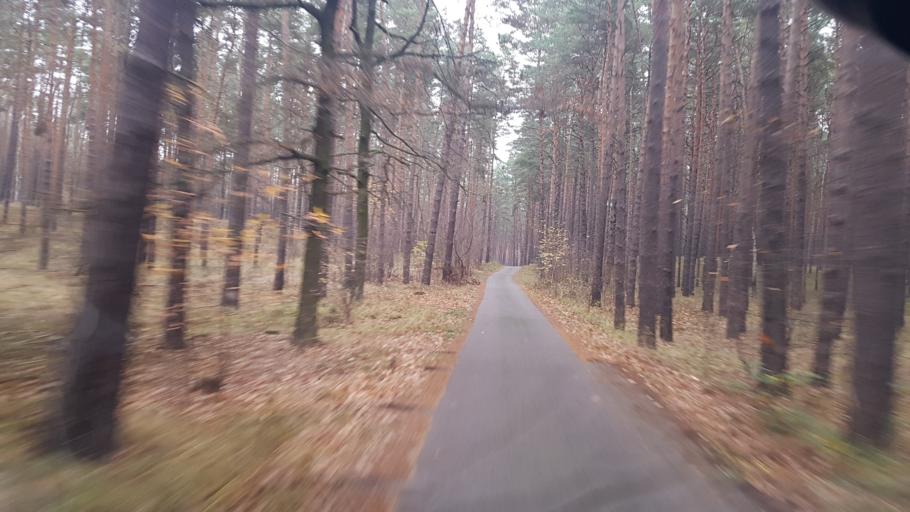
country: DE
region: Brandenburg
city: Schenkendobern
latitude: 51.9770
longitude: 14.6553
